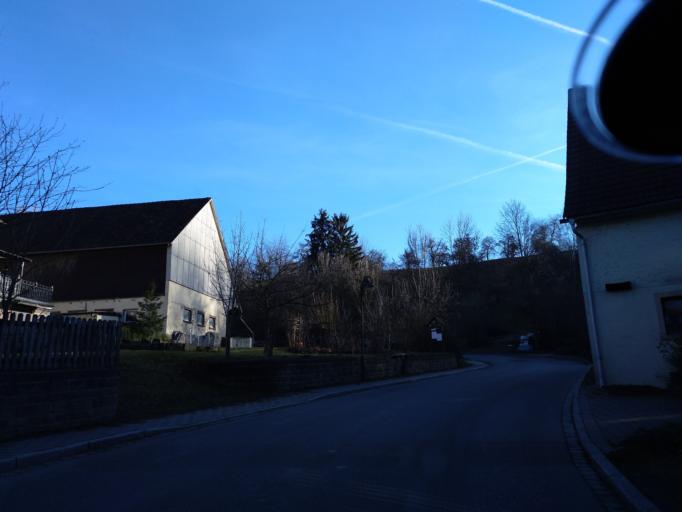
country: DE
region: Baden-Wuerttemberg
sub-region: Regierungsbezirk Stuttgart
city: Vellberg
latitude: 49.0825
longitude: 9.8956
